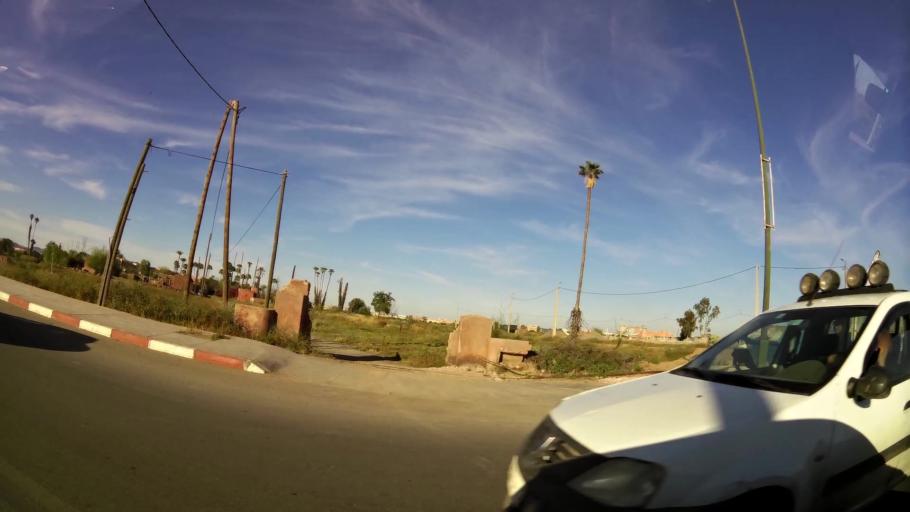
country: MA
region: Marrakech-Tensift-Al Haouz
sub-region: Marrakech
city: Marrakesh
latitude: 31.6670
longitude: -8.0573
